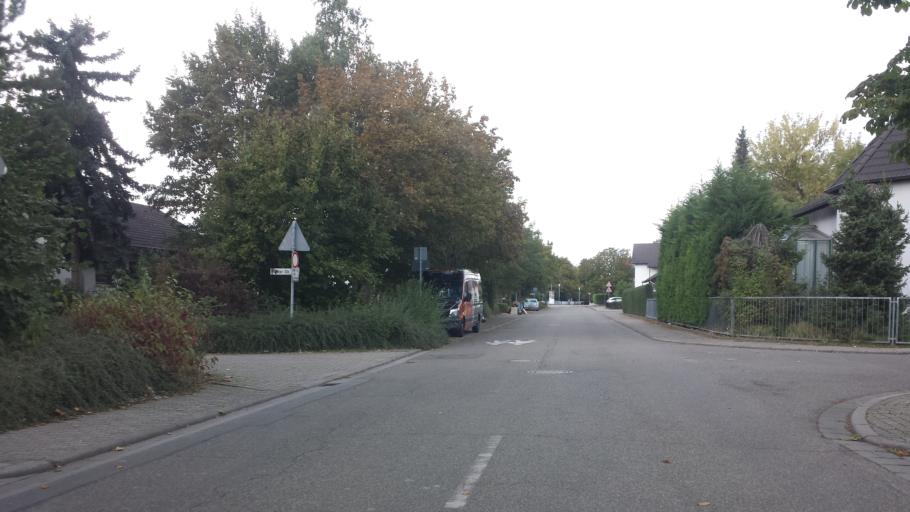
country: DE
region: Rheinland-Pfalz
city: Dannstadt-Schauernheim
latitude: 49.4249
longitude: 8.3140
